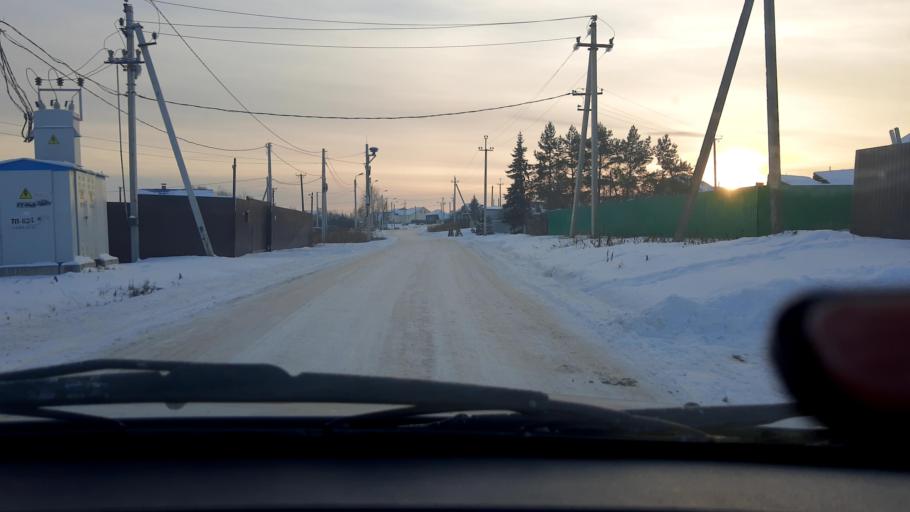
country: RU
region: Bashkortostan
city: Mikhaylovka
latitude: 54.7472
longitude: 55.7987
